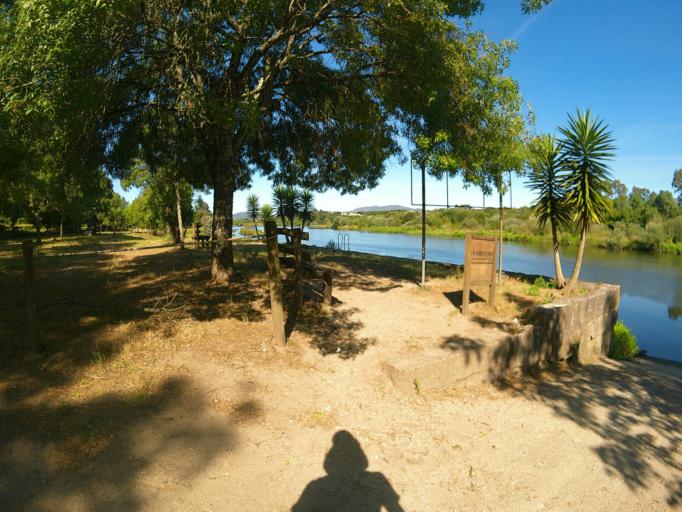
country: PT
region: Viana do Castelo
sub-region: Ponte de Lima
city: Ponte de Lima
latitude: 41.7361
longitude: -8.6535
